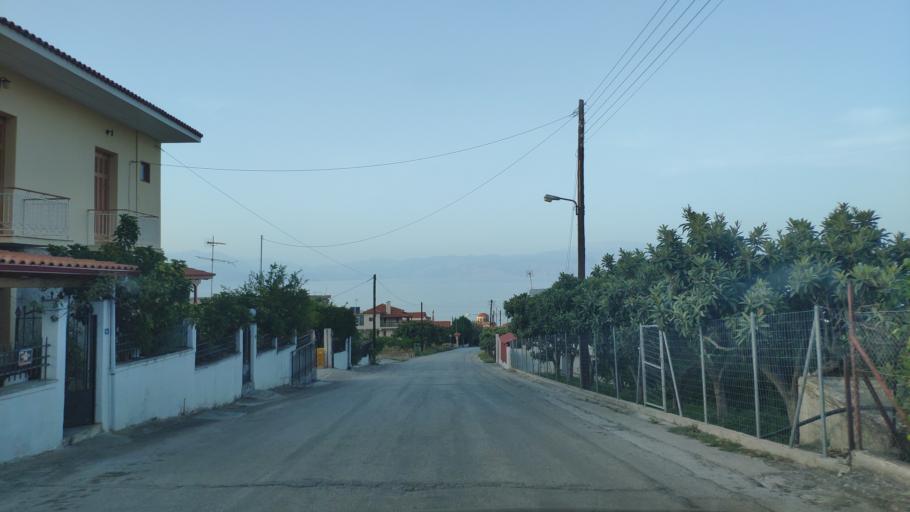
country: GR
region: West Greece
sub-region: Nomos Achaias
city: Aiyira
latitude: 38.1260
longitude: 22.3993
